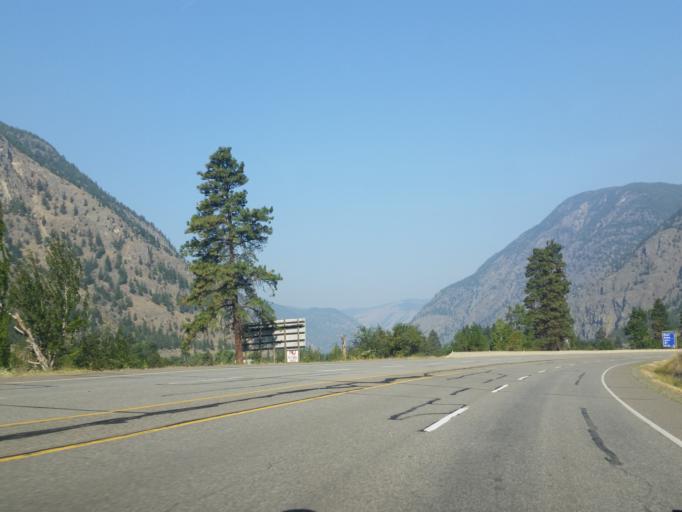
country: CA
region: British Columbia
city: Oliver
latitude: 49.2052
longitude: -119.8884
